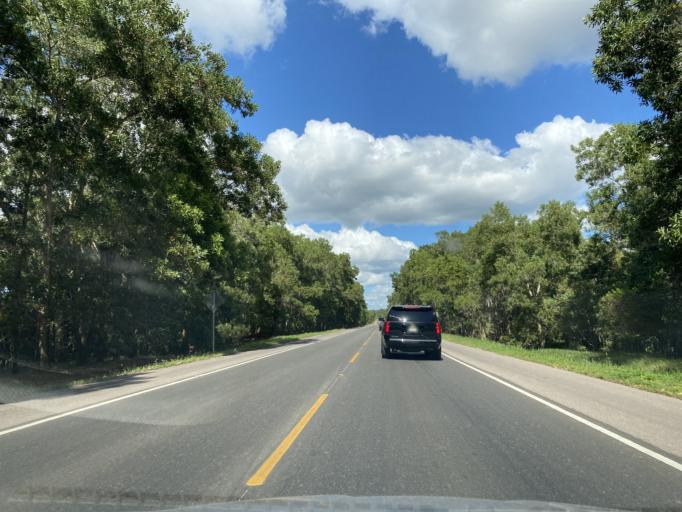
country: DO
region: Monte Plata
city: Monte Plata
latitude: 18.7524
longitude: -69.7657
